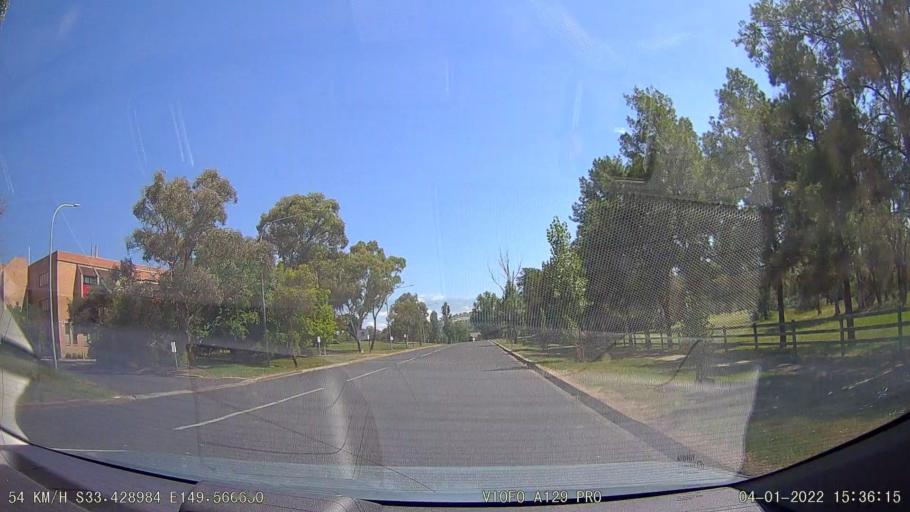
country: AU
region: New South Wales
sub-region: Bathurst Regional
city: Bathurst
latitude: -33.4288
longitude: 149.5668
